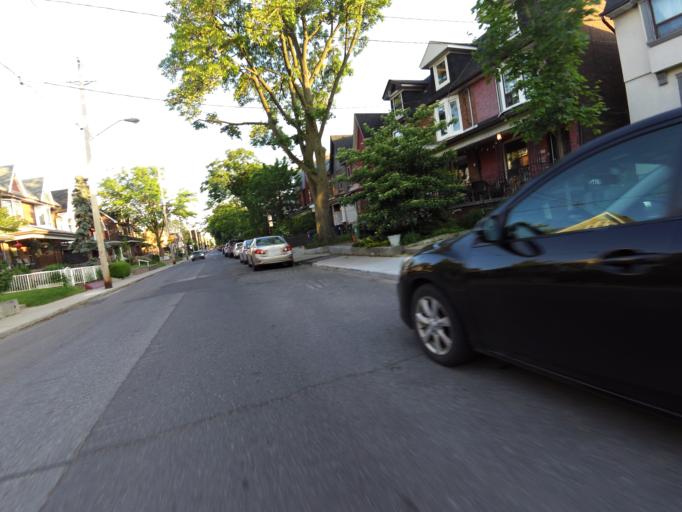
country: CA
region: Ontario
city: Toronto
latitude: 43.6559
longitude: -79.4380
